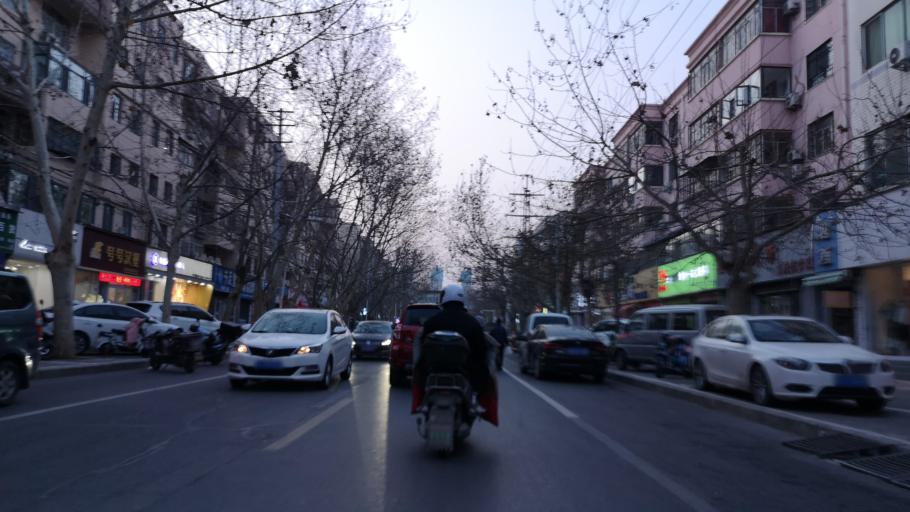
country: CN
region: Henan Sheng
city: Zhongyuanlu
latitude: 35.7660
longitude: 115.0660
